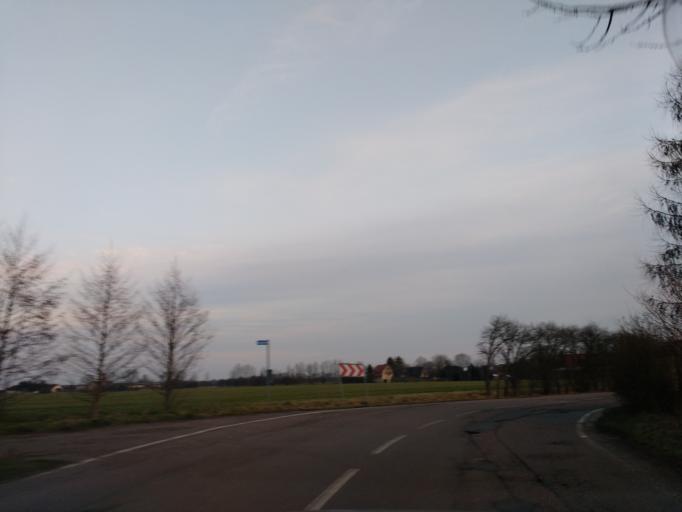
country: DE
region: Saxony-Anhalt
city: Halle (Saale)
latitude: 51.5214
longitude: 12.0109
